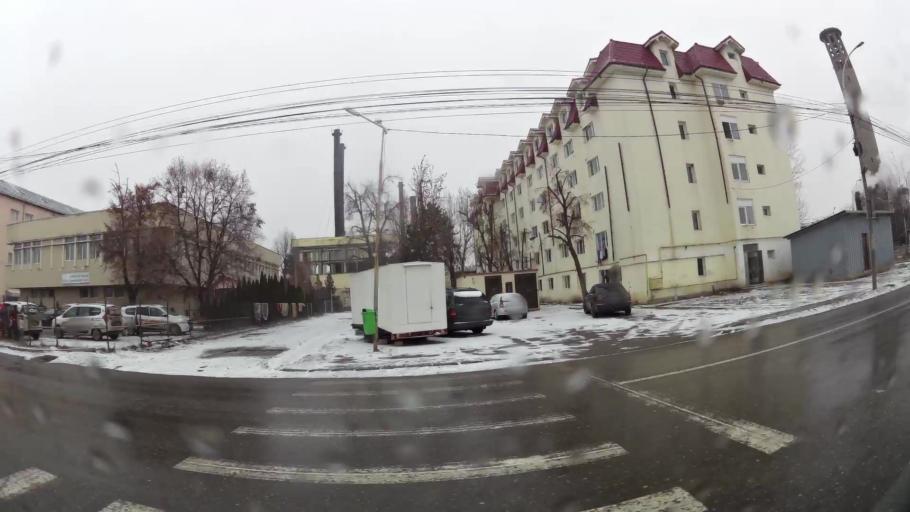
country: RO
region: Dambovita
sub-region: Municipiul Targoviste
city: Targoviste
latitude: 44.9154
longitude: 25.4414
